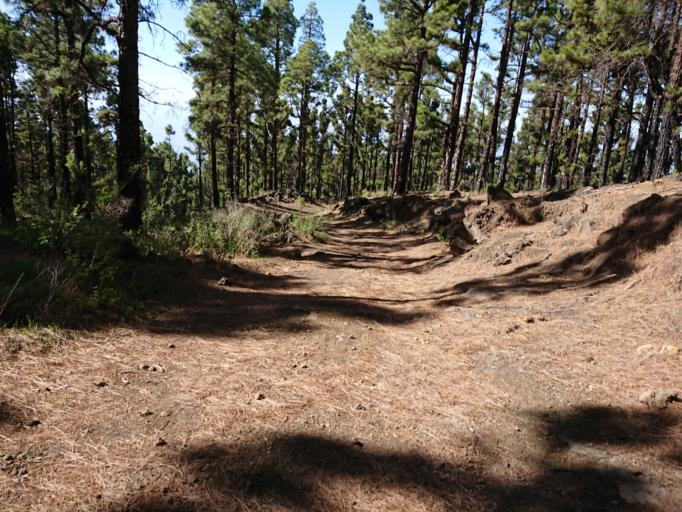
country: ES
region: Canary Islands
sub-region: Provincia de Santa Cruz de Tenerife
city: El Paso
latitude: 28.5931
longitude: -17.8608
